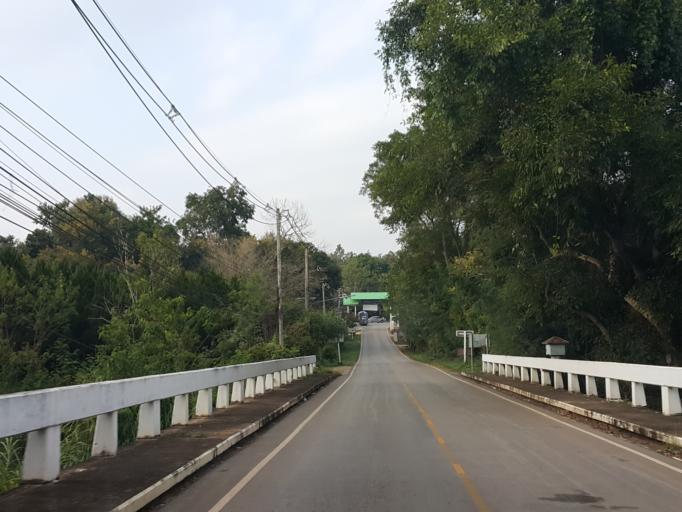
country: TH
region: Chiang Mai
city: Mae On
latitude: 18.9160
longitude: 99.2359
